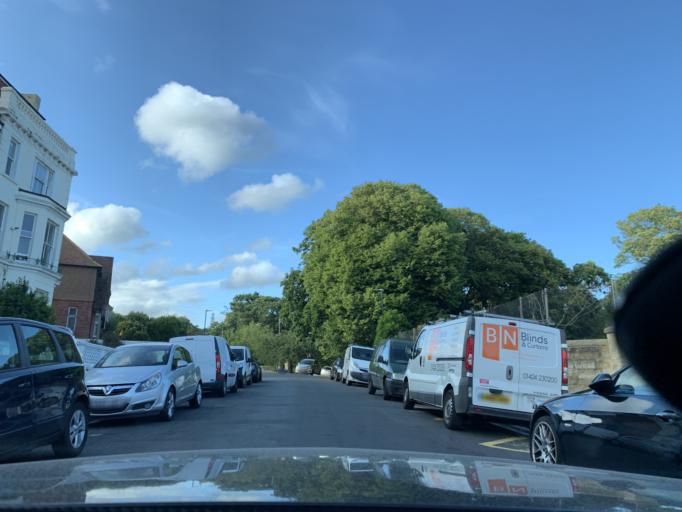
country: GB
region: England
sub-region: East Sussex
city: Hastings
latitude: 50.8571
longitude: 0.5655
